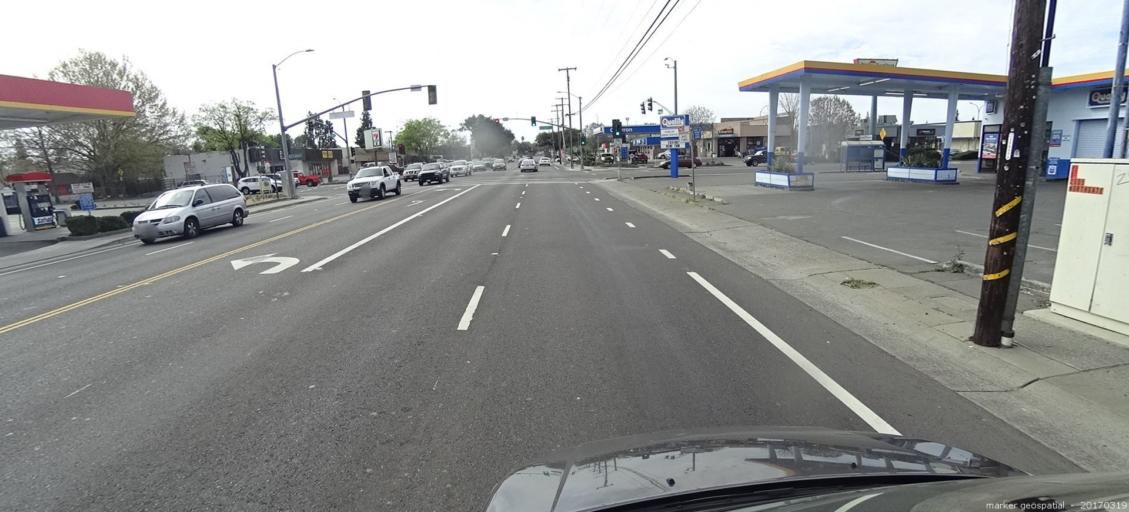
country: US
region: California
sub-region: Sacramento County
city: Sacramento
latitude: 38.6118
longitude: -121.4756
